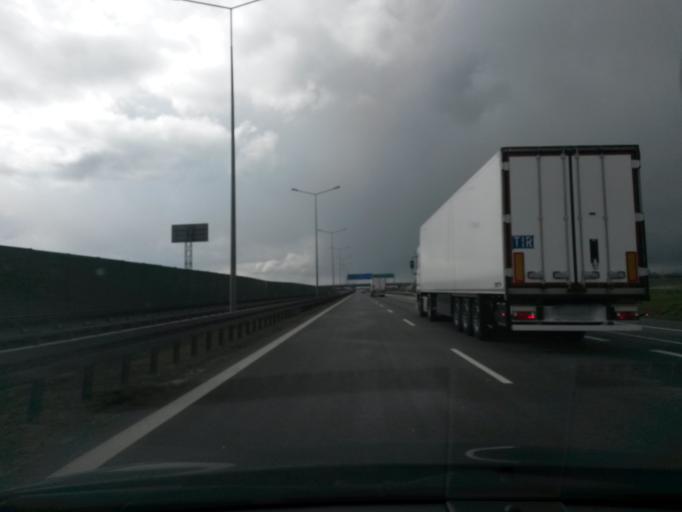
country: PL
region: Greater Poland Voivodeship
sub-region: Powiat poznanski
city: Kleszczewo
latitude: 52.3153
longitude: 17.1363
